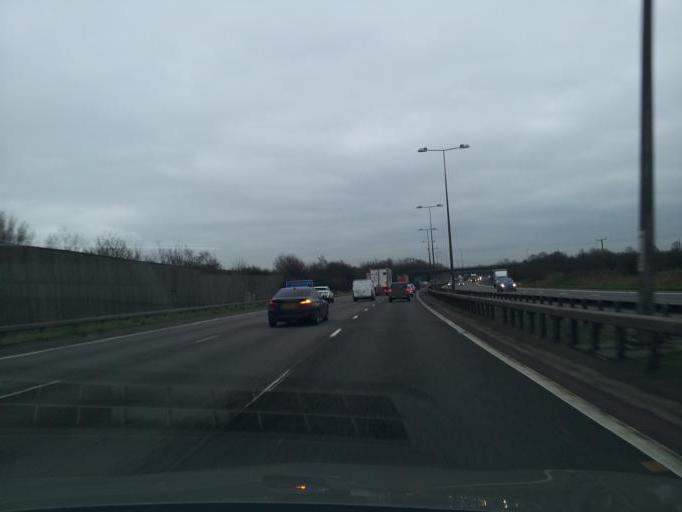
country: GB
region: England
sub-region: Derbyshire
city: Long Eaton
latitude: 52.9022
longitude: -1.2989
